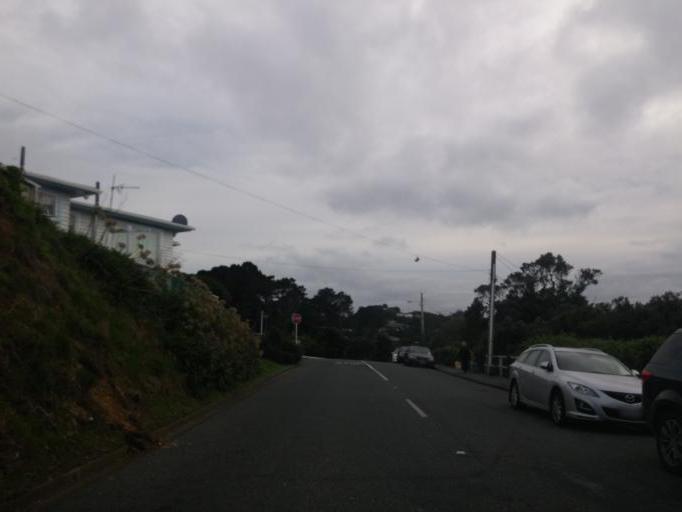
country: NZ
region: Wellington
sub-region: Wellington City
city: Brooklyn
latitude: -41.3207
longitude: 174.7685
